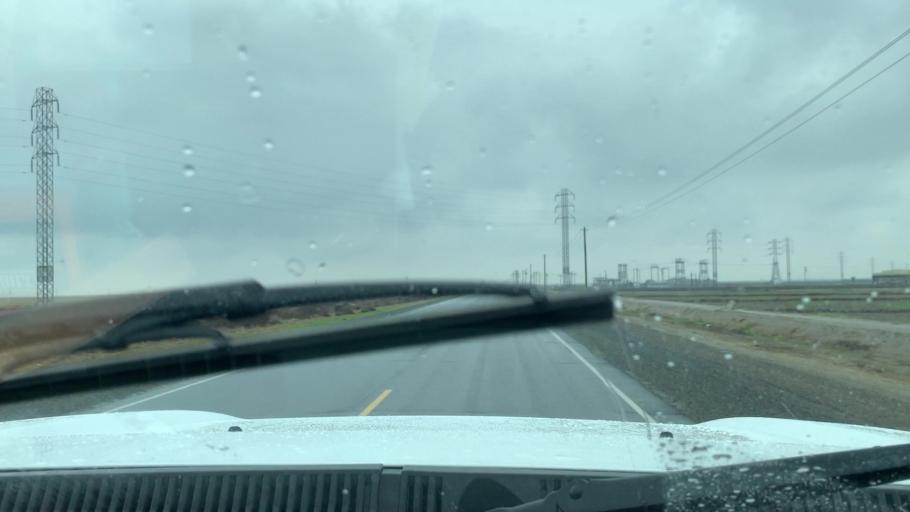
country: US
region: California
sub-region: Tulare County
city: Alpaugh
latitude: 35.9595
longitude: -119.4550
